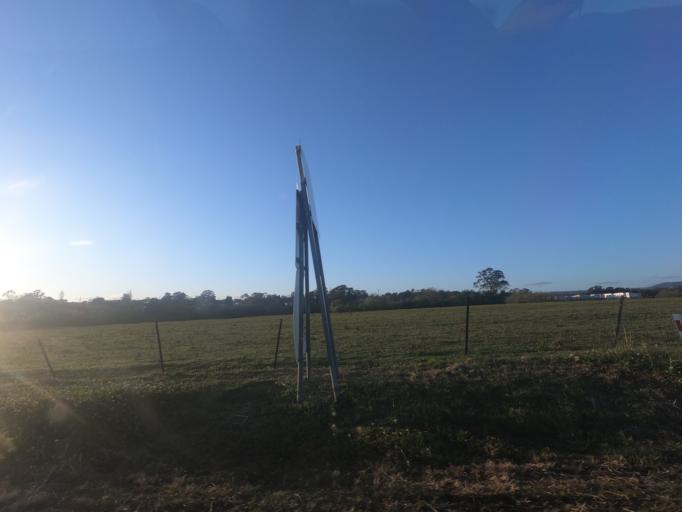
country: AU
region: New South Wales
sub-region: Wollongong
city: Dapto
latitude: -34.5024
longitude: 150.7825
